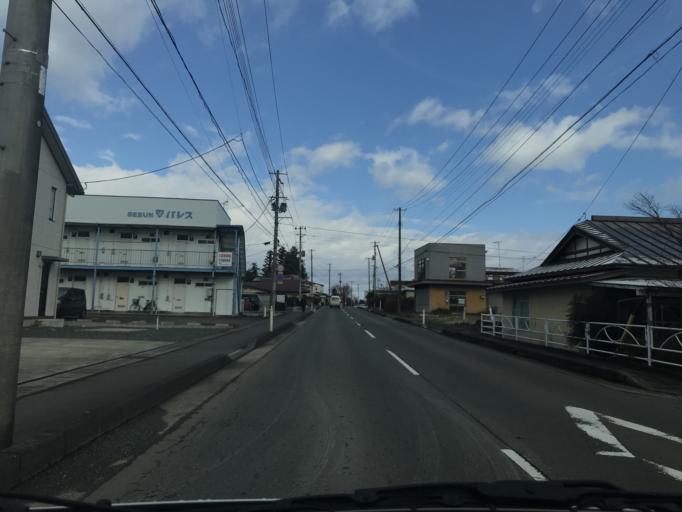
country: JP
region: Iwate
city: Mizusawa
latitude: 39.1160
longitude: 141.1377
